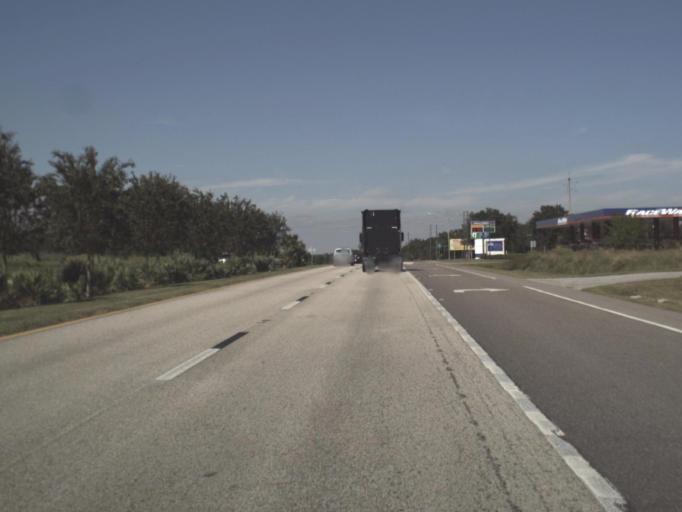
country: US
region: Florida
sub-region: Highlands County
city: Lake Placid
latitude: 27.3090
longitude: -81.3586
